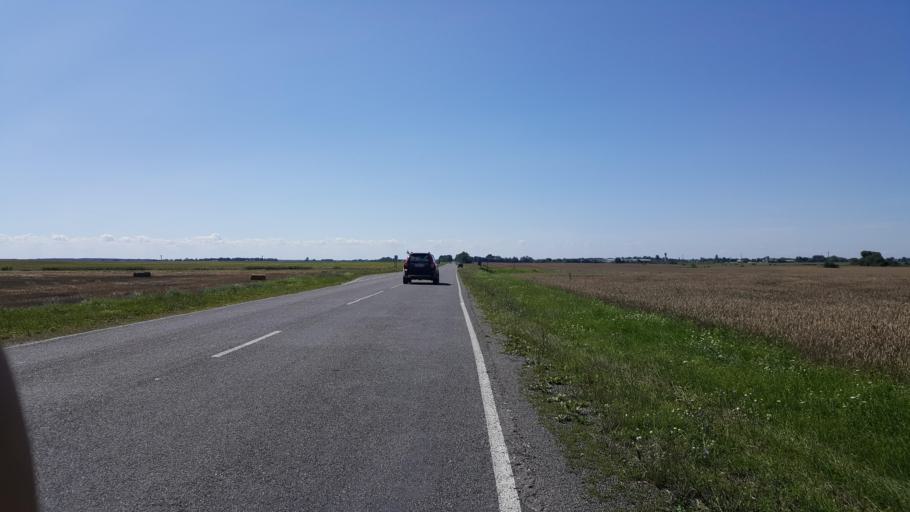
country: BY
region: Brest
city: Charnawchytsy
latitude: 52.2057
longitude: 23.7939
